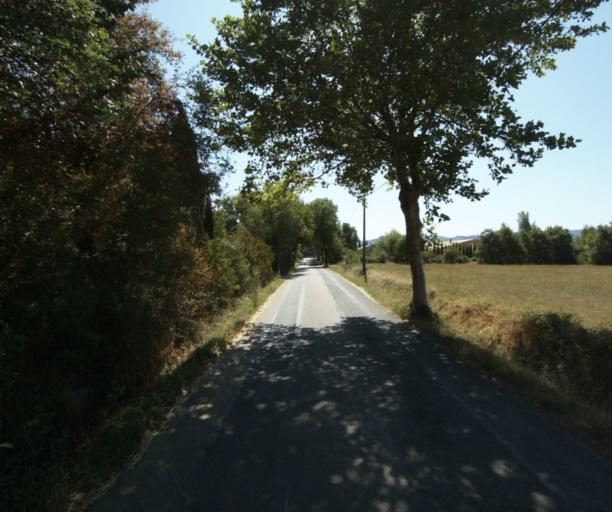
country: FR
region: Midi-Pyrenees
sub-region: Departement de la Haute-Garonne
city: Revel
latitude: 43.4667
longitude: 2.0054
